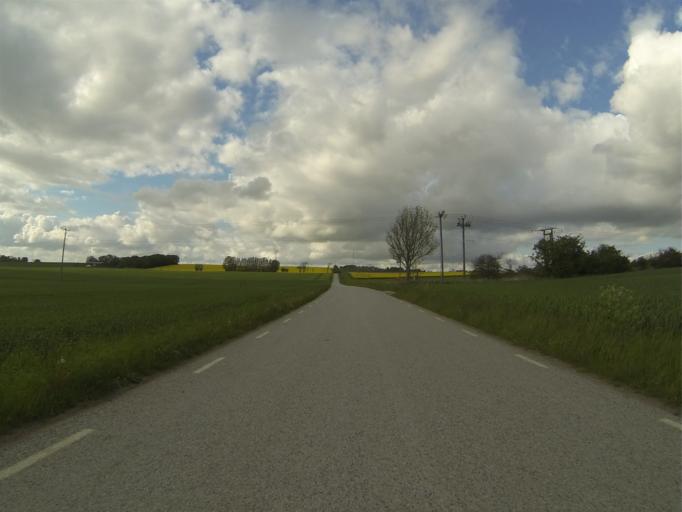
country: SE
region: Skane
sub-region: Staffanstorps Kommun
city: Staffanstorp
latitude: 55.6867
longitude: 13.2872
